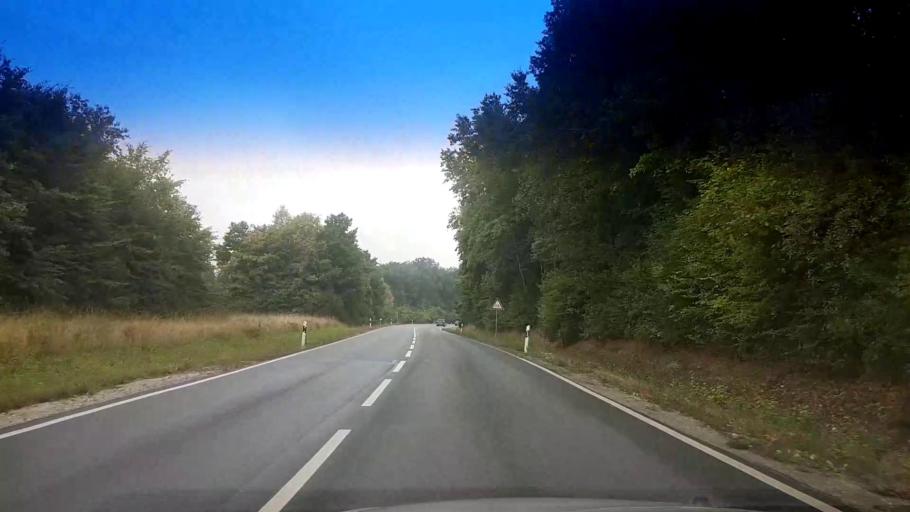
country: DE
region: Bavaria
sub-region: Upper Franconia
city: Forchheim
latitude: 49.7113
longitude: 11.0413
